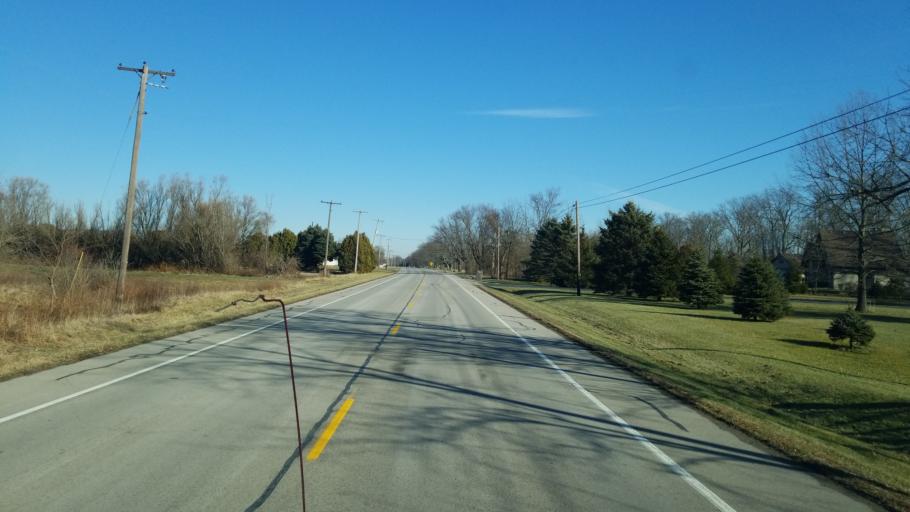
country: US
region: Ohio
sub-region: Lucas County
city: Whitehouse
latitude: 41.4407
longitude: -83.8113
